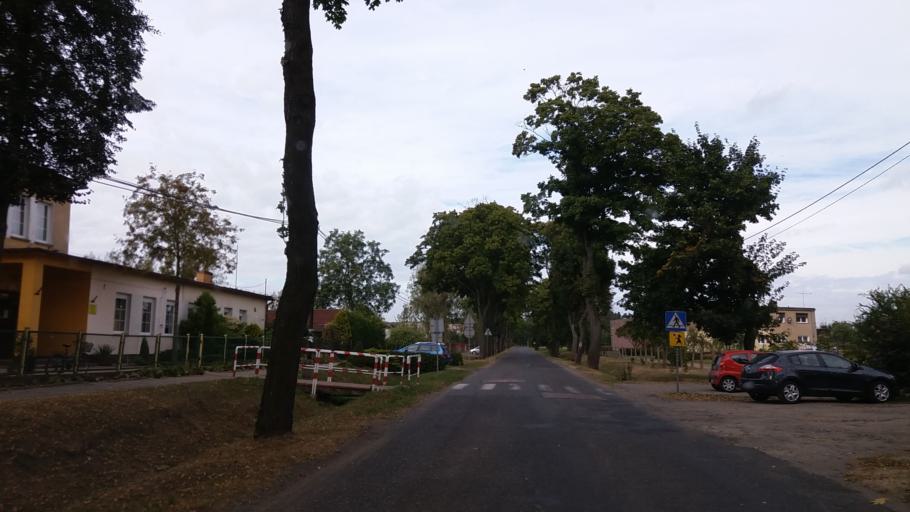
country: PL
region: Lubusz
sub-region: Powiat strzelecko-drezdenecki
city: Strzelce Krajenskie
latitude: 52.9552
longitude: 15.4527
